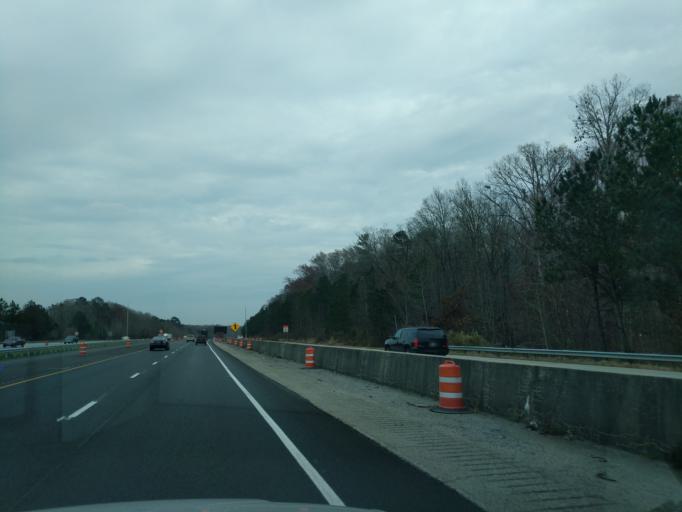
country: US
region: Georgia
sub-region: Gwinnett County
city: Sugar Hill
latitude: 34.0567
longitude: -83.9945
